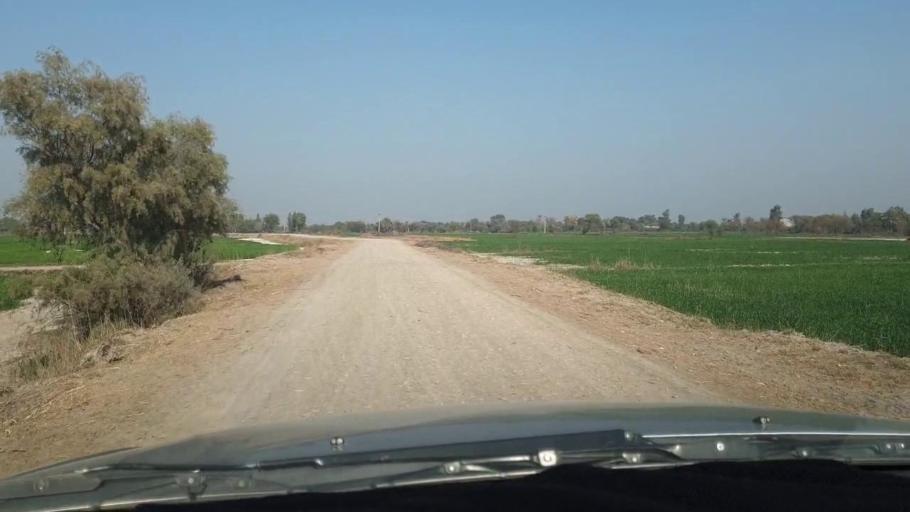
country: PK
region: Sindh
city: Mirpur Mathelo
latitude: 27.9155
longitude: 69.5556
